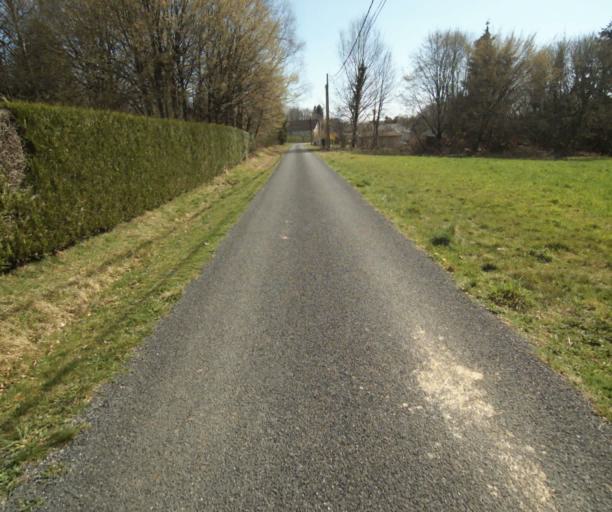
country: FR
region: Limousin
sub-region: Departement de la Correze
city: Saint-Clement
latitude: 45.3123
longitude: 1.6779
